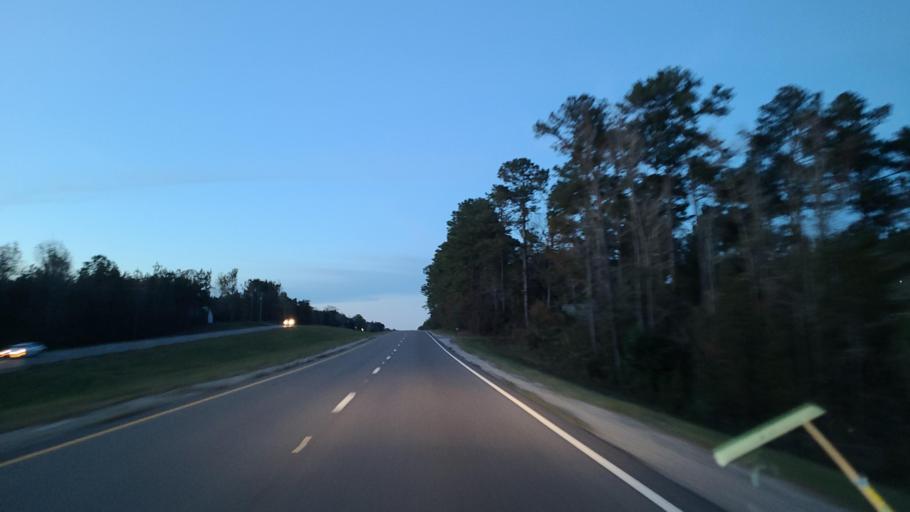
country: US
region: Mississippi
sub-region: Forrest County
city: Hattiesburg
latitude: 31.2059
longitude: -89.2593
